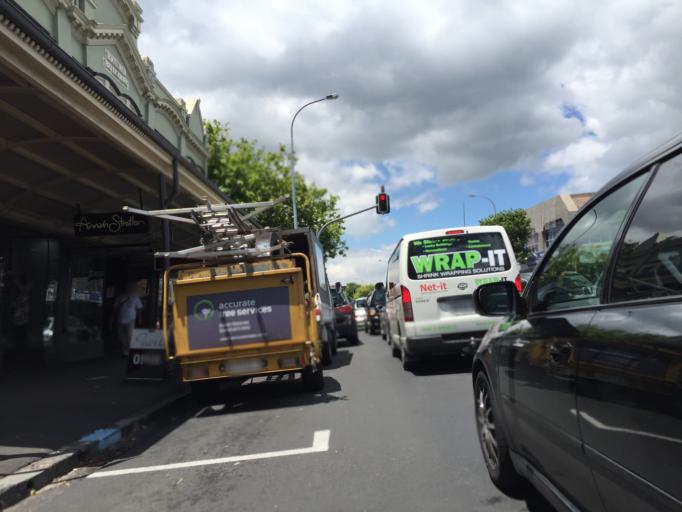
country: NZ
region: Auckland
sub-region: Auckland
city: Auckland
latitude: -36.8529
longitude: 174.7454
